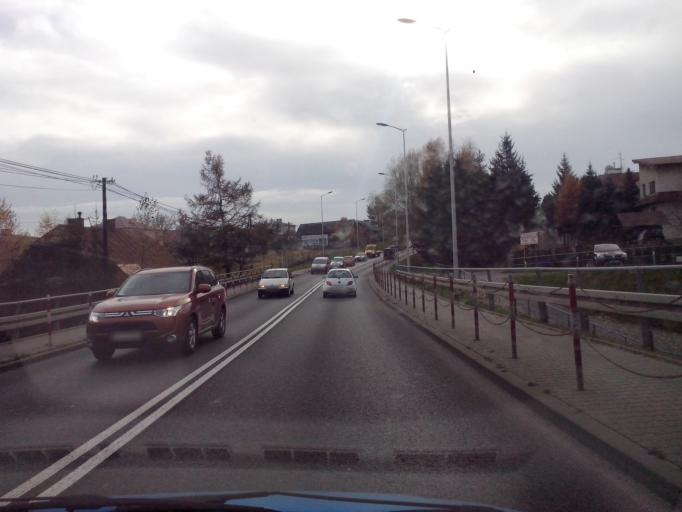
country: PL
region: Subcarpathian Voivodeship
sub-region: Powiat rzeszowski
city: Boguchwala
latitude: 50.0044
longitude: 21.9584
